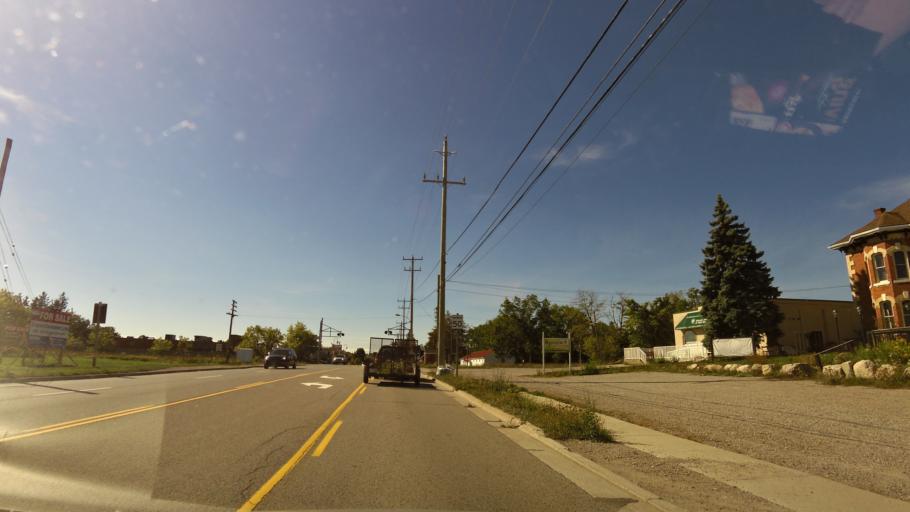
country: CA
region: Ontario
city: Ancaster
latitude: 43.0786
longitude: -79.9497
